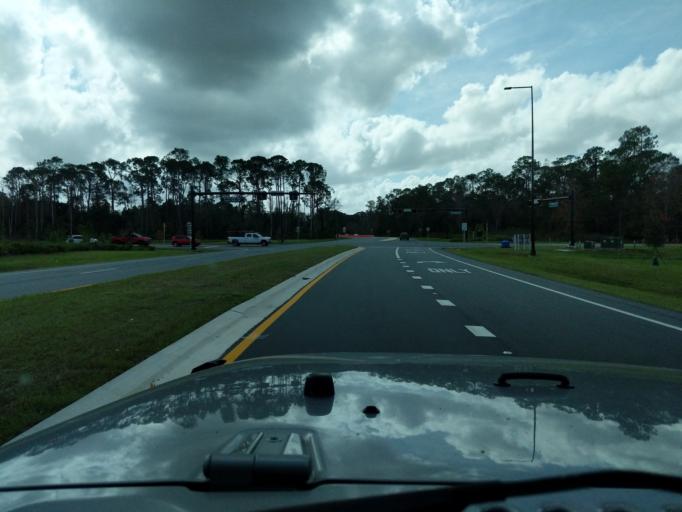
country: US
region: Florida
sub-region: Orange County
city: Bay Hill
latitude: 28.4188
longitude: -81.5897
